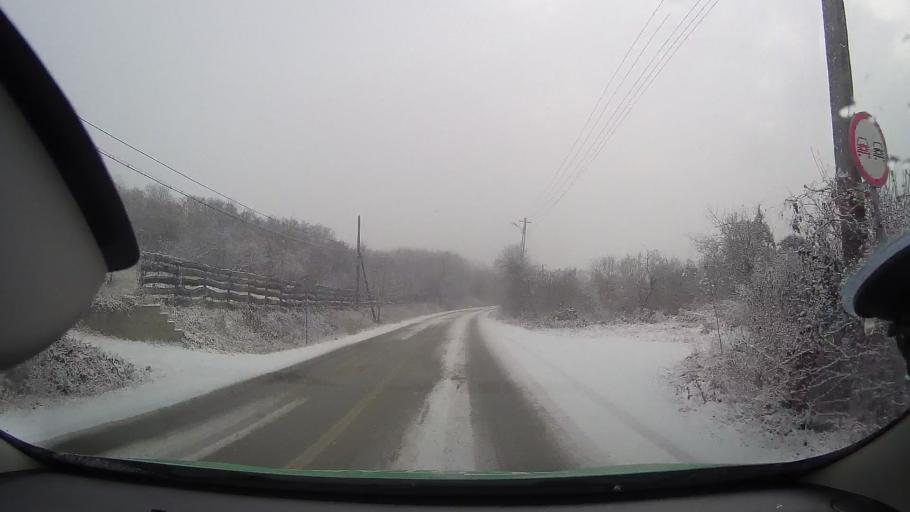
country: RO
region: Alba
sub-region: Municipiul Aiud
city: Aiudul de Sus
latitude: 46.3400
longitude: 23.6676
